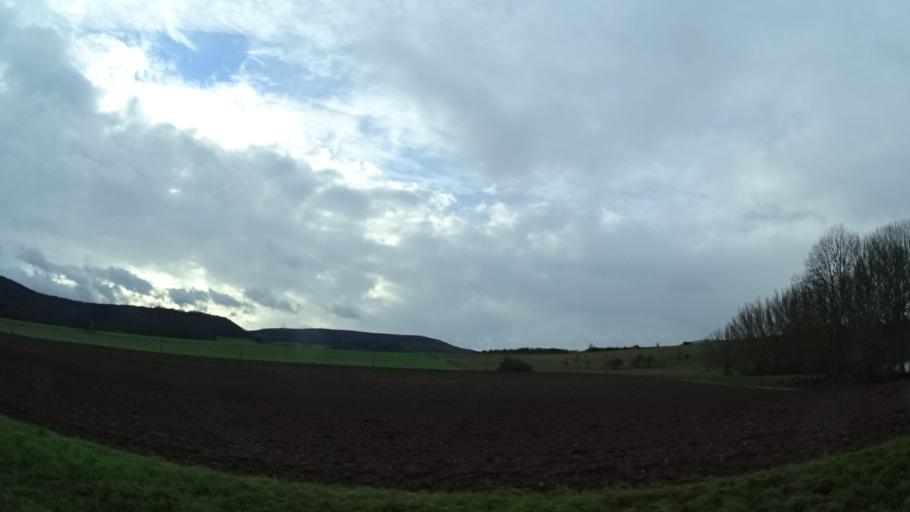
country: DE
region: Thuringia
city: Stepfershausen
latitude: 50.5699
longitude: 10.3068
